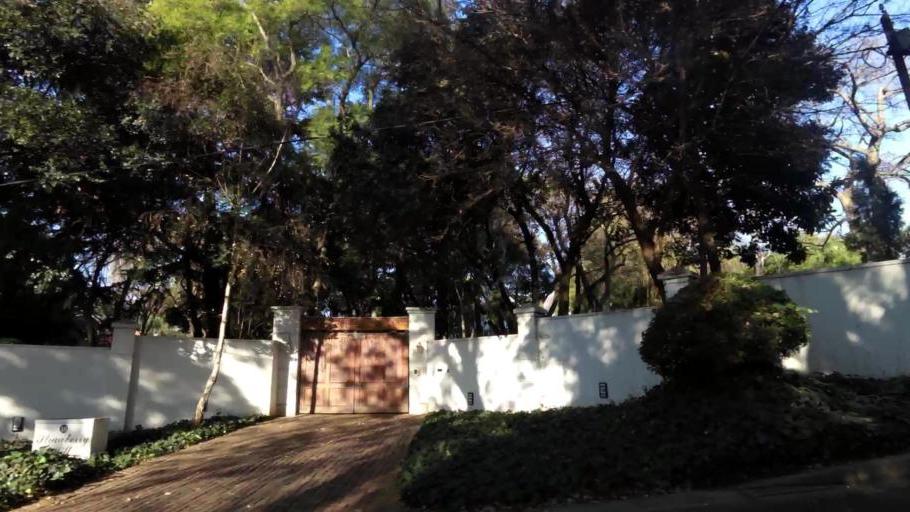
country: ZA
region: Gauteng
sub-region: City of Johannesburg Metropolitan Municipality
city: Johannesburg
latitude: -26.1873
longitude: 27.9983
